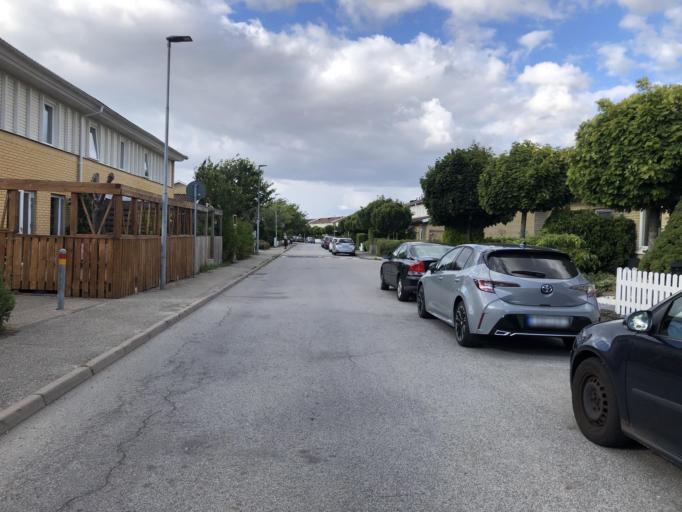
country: SE
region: Skane
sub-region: Malmo
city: Malmoe
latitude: 55.5713
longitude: 13.0270
